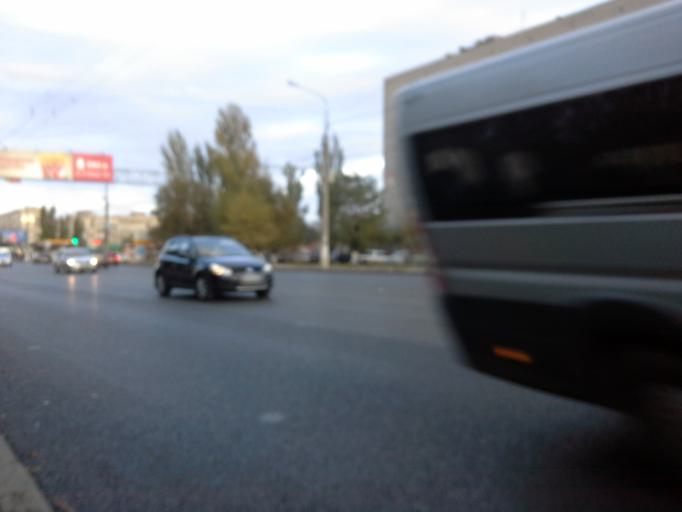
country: RU
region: Volgograd
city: Vodstroy
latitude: 48.8194
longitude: 44.6319
